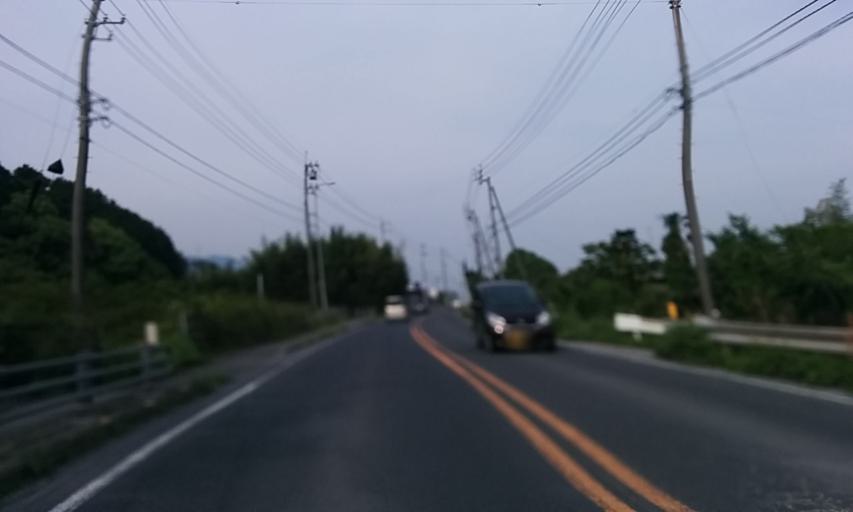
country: JP
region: Ehime
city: Niihama
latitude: 33.9587
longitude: 133.4416
